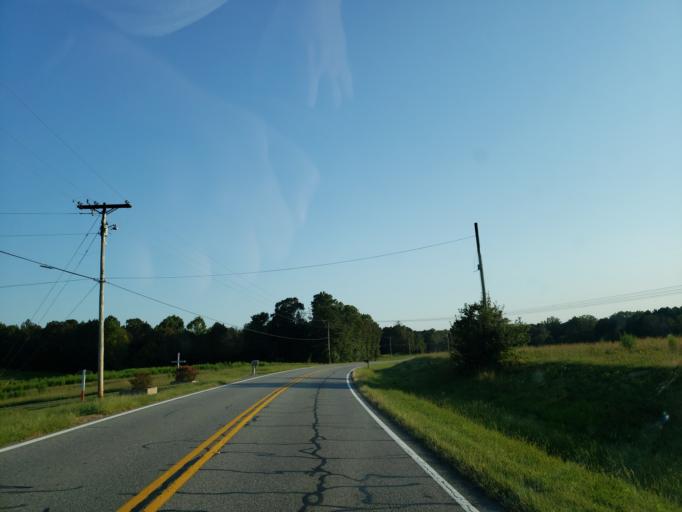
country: US
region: Georgia
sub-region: Gordon County
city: Calhoun
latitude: 34.5561
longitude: -84.8931
